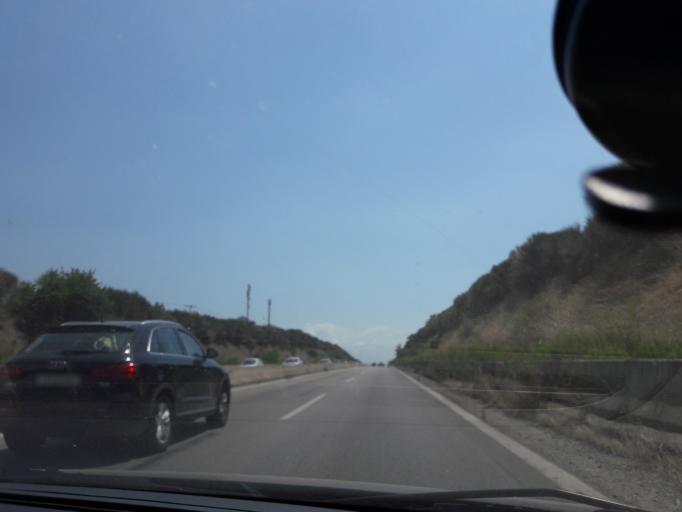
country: GR
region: Central Macedonia
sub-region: Nomos Chalkidikis
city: Nea Triglia
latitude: 40.2999
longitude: 23.1356
